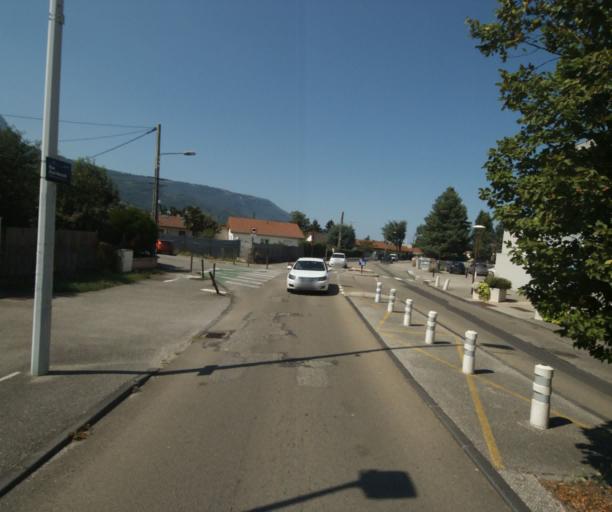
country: FR
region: Rhone-Alpes
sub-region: Departement de l'Isere
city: Echirolles
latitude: 45.1486
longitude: 5.7121
